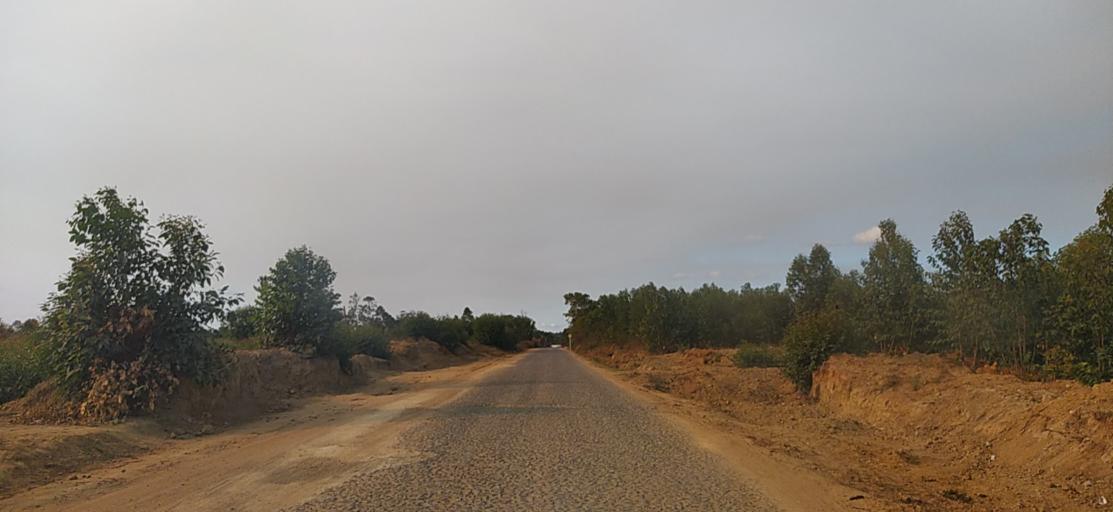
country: MG
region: Alaotra Mangoro
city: Moramanga
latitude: -18.6167
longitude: 48.2770
